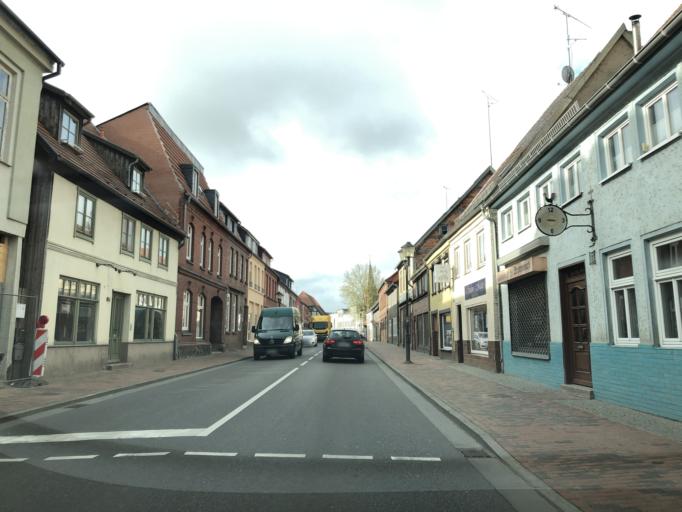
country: DE
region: Mecklenburg-Vorpommern
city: Goldberg
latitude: 53.5891
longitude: 12.0883
